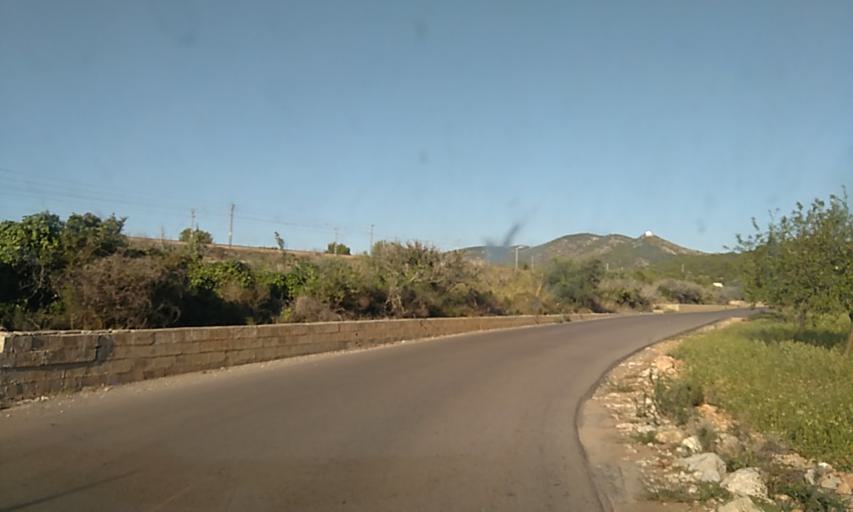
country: ES
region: Valencia
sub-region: Provincia de Castello
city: Alcoceber
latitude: 40.2481
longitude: 0.2420
